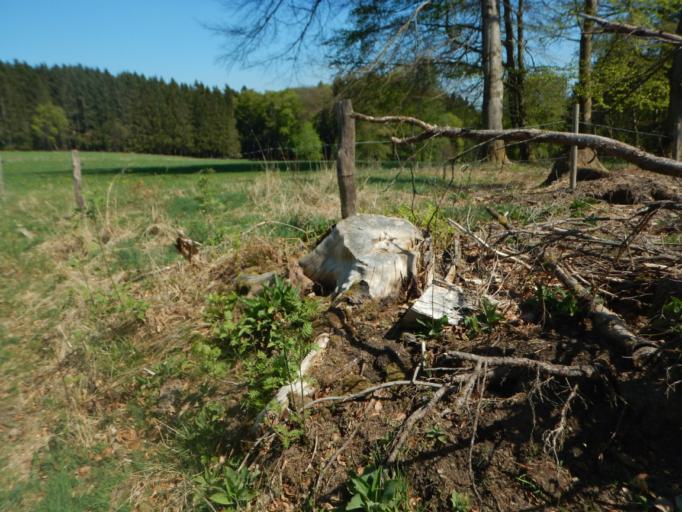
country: LU
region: Diekirch
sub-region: Canton de Clervaux
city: Weiswampach
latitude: 50.1528
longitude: 6.0397
